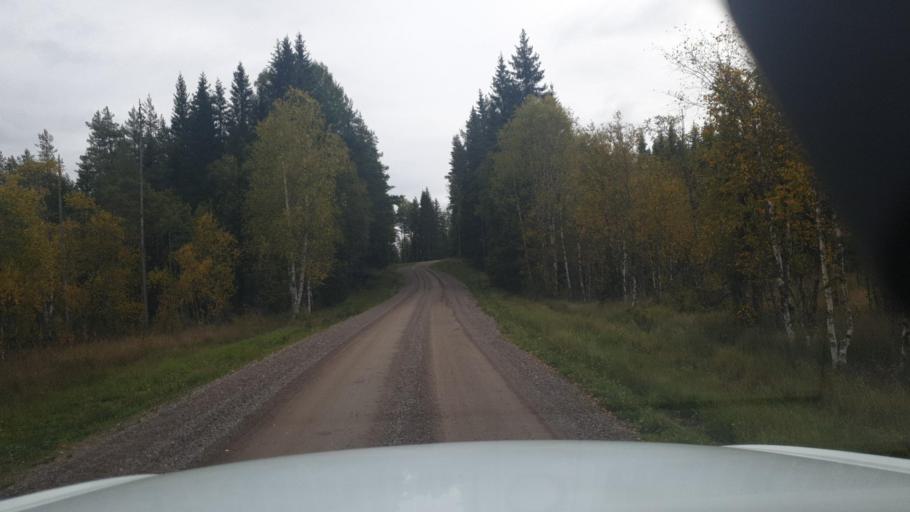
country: SE
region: Vaermland
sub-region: Eda Kommun
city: Charlottenberg
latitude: 60.0500
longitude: 12.5691
